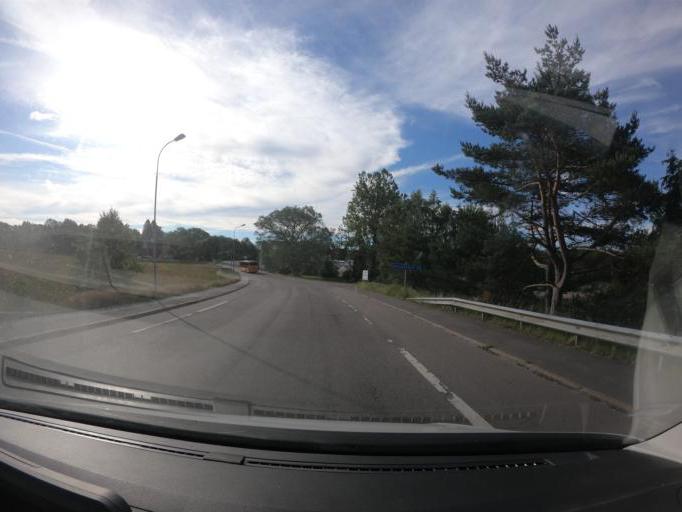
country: SE
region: Skane
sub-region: Orkelljunga Kommun
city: OErkelljunga
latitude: 56.2774
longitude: 13.2815
